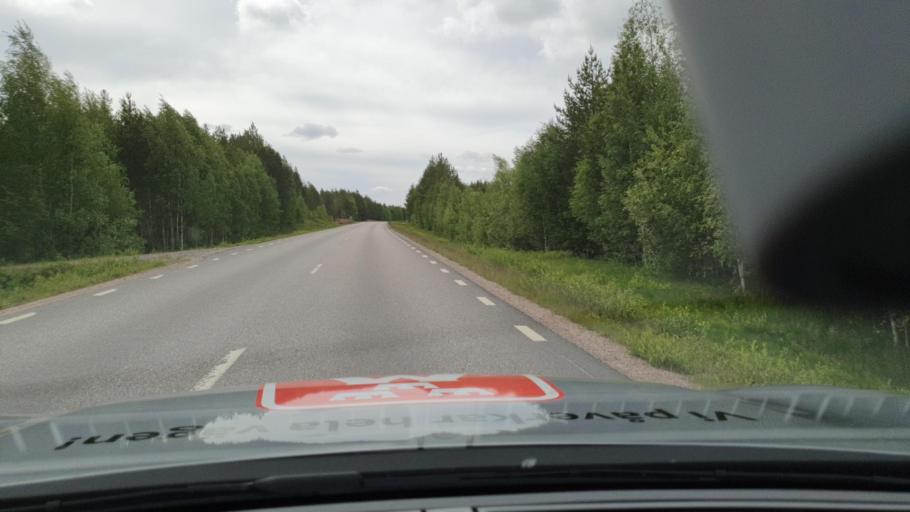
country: SE
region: Norrbotten
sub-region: Kalix Kommun
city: Kalix
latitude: 65.8608
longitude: 23.4810
